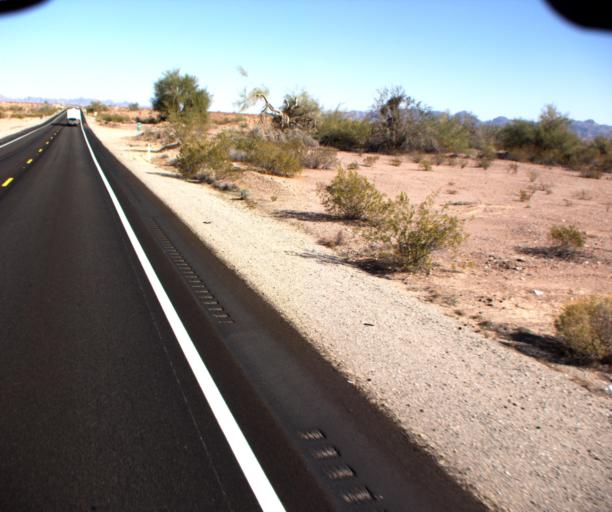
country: US
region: Arizona
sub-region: Yuma County
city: Wellton
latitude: 33.0478
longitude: -114.2908
